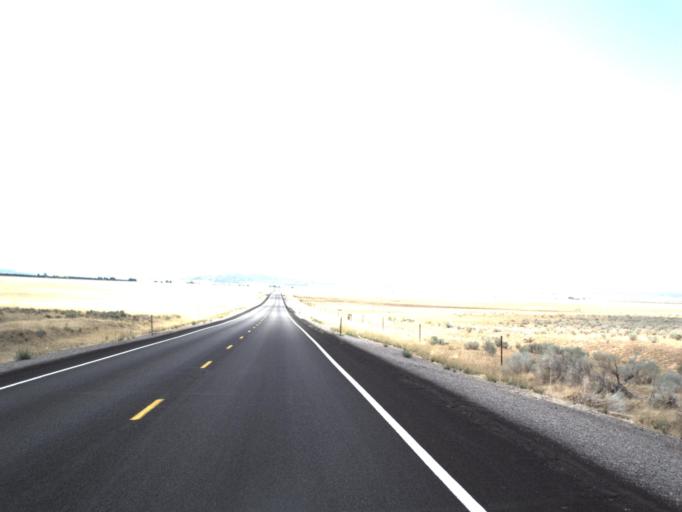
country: US
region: Utah
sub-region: Millard County
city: Fillmore
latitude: 39.1370
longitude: -112.2448
